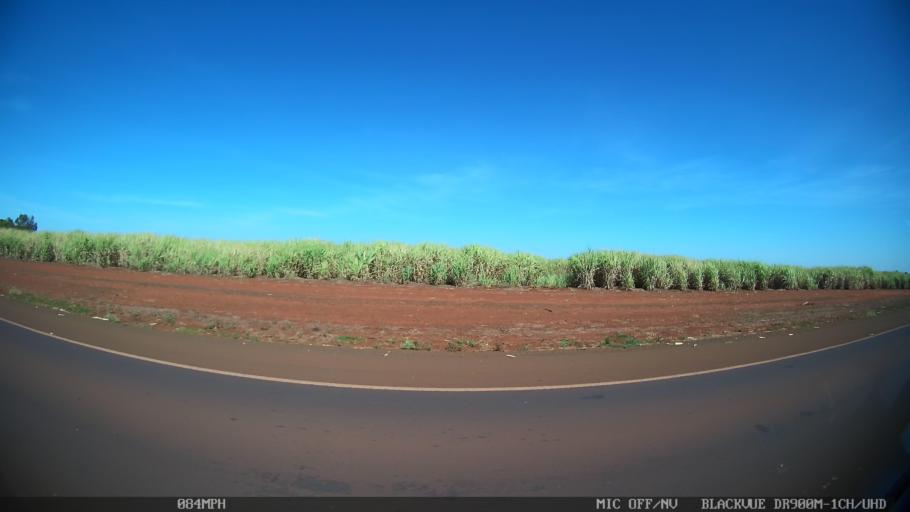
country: BR
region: Sao Paulo
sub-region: Guaira
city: Guaira
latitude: -20.4439
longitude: -48.2933
